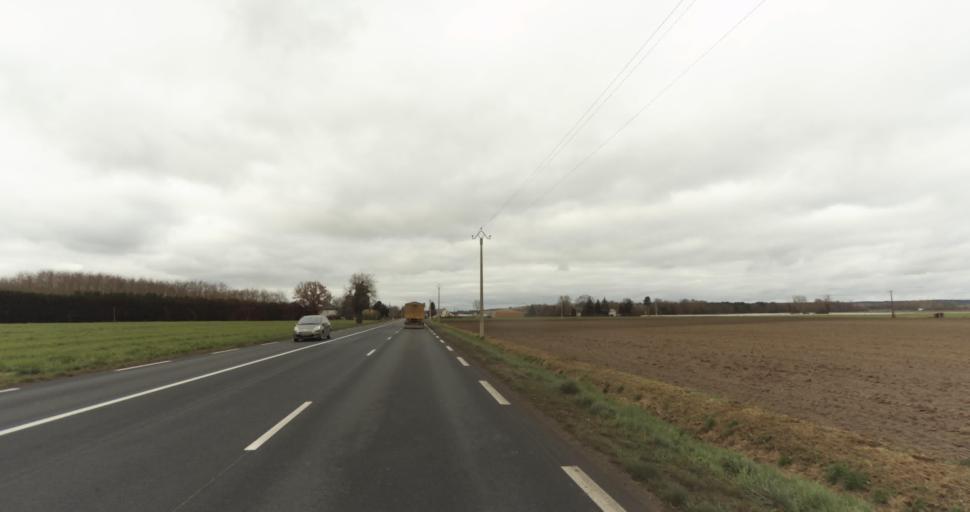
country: FR
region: Pays de la Loire
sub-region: Departement de Maine-et-Loire
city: Vivy
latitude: 47.3097
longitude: -0.0404
